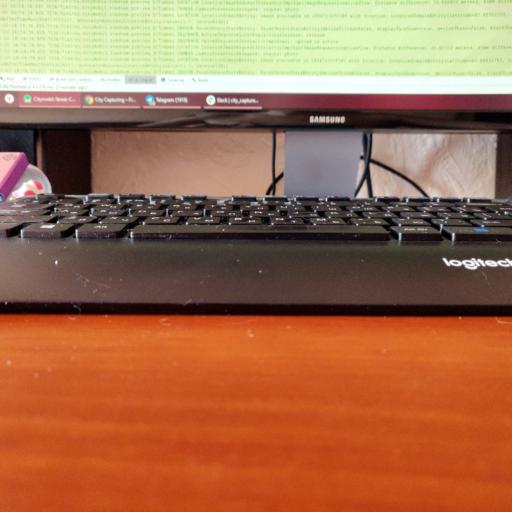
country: FI
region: Varsinais-Suomi
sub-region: Salo
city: Somero
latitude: 60.6311
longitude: 23.4636
